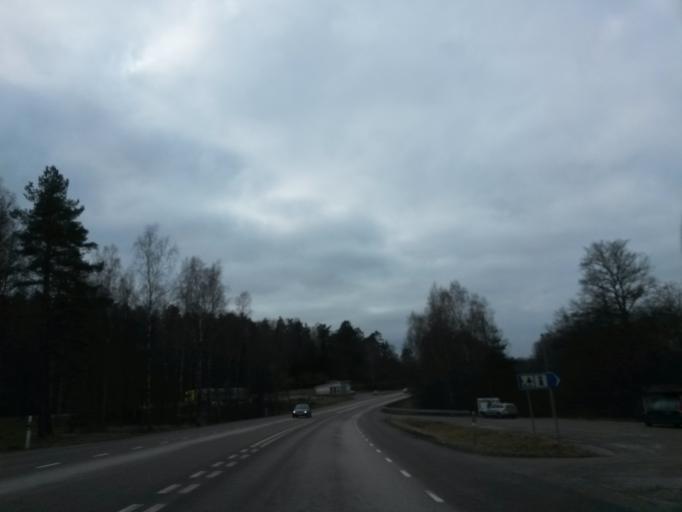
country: SE
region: Vaestra Goetaland
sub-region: Alingsas Kommun
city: Alingsas
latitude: 57.9354
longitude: 12.5781
